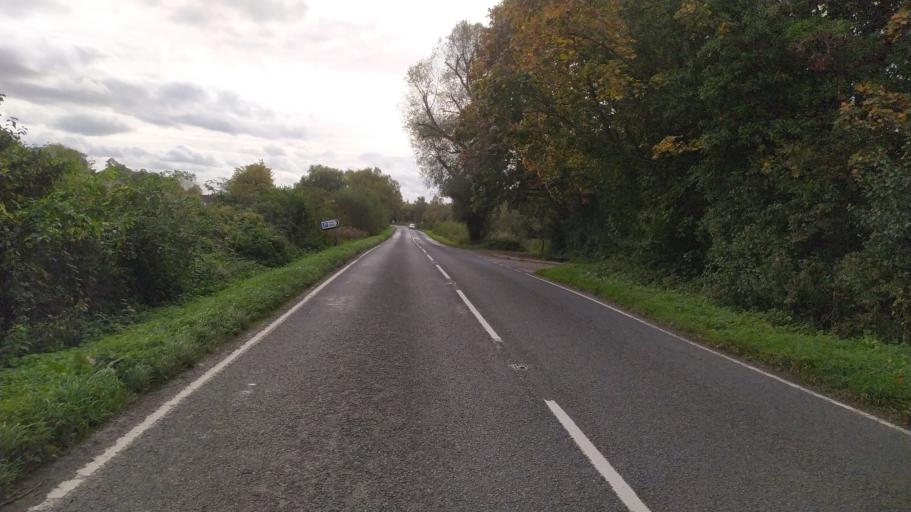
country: GB
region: England
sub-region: Hampshire
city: Romsey
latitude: 51.0409
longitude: -1.5228
